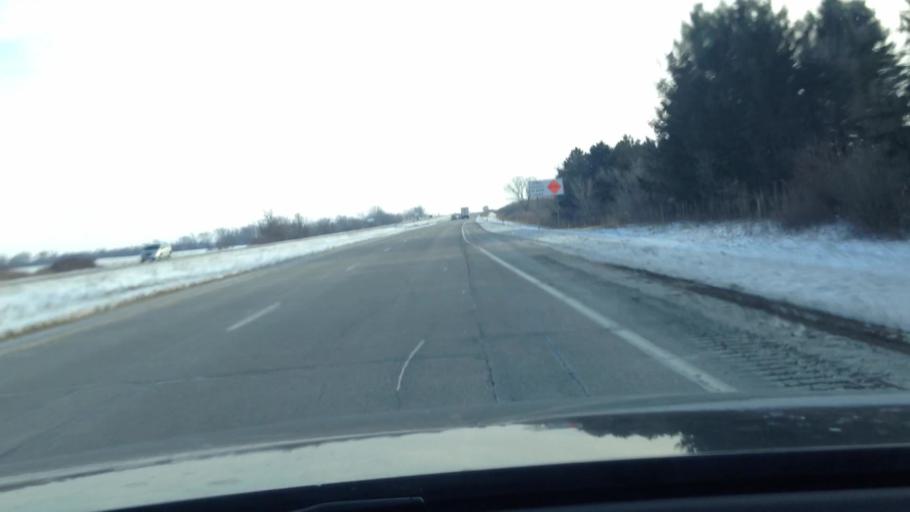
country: US
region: Wisconsin
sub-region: Walworth County
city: Elkhorn
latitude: 42.6619
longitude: -88.5132
